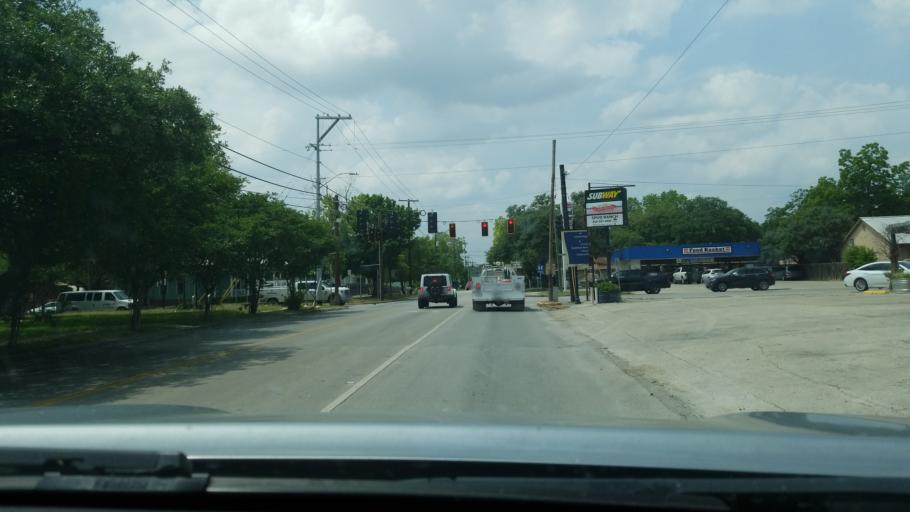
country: US
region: Texas
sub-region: Comal County
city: New Braunfels
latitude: 29.7095
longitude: -98.1194
